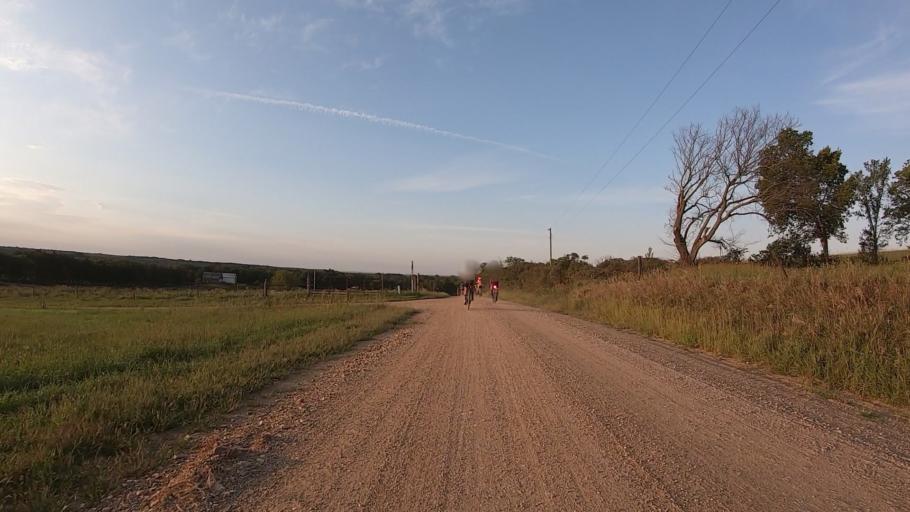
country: US
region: Kansas
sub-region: Marshall County
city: Marysville
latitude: 39.7912
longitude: -96.6837
